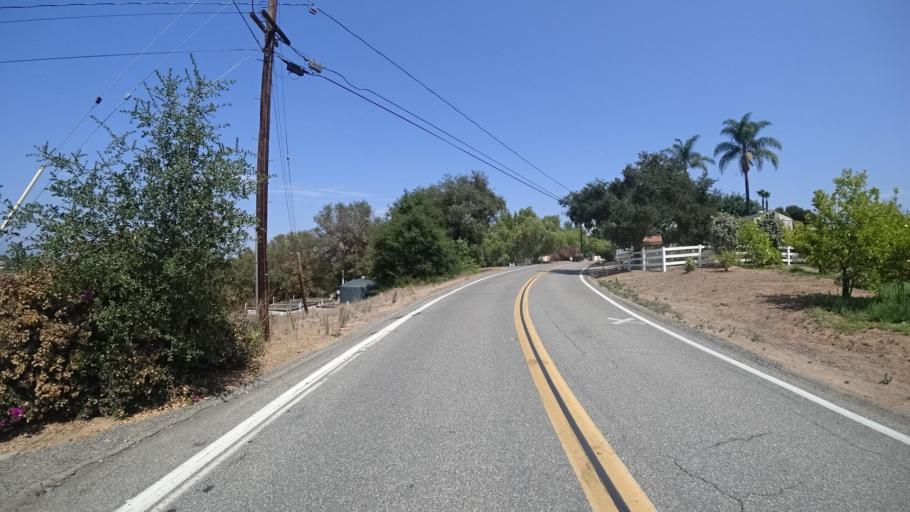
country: US
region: California
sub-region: San Diego County
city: Fallbrook
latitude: 33.3387
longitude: -117.2270
